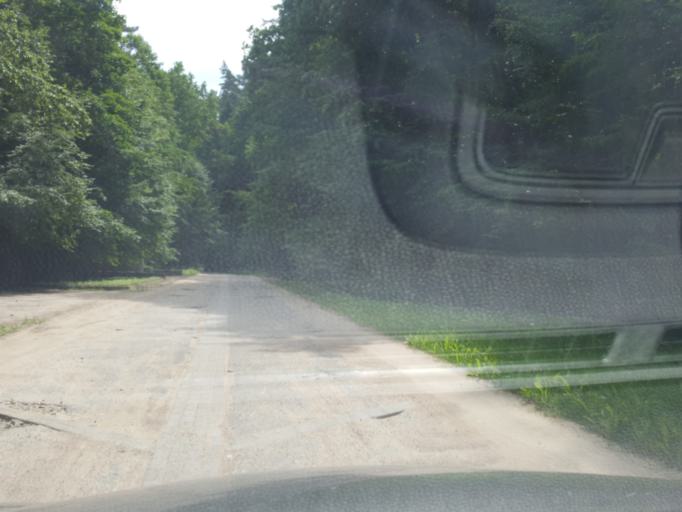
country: LT
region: Alytaus apskritis
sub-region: Alytus
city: Alytus
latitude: 54.3786
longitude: 24.0423
